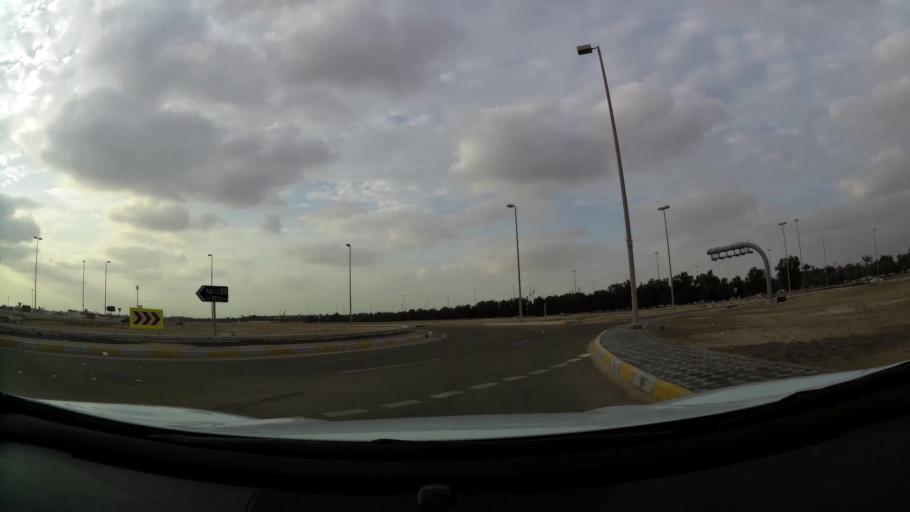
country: AE
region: Abu Dhabi
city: Abu Dhabi
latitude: 24.3834
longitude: 54.5426
